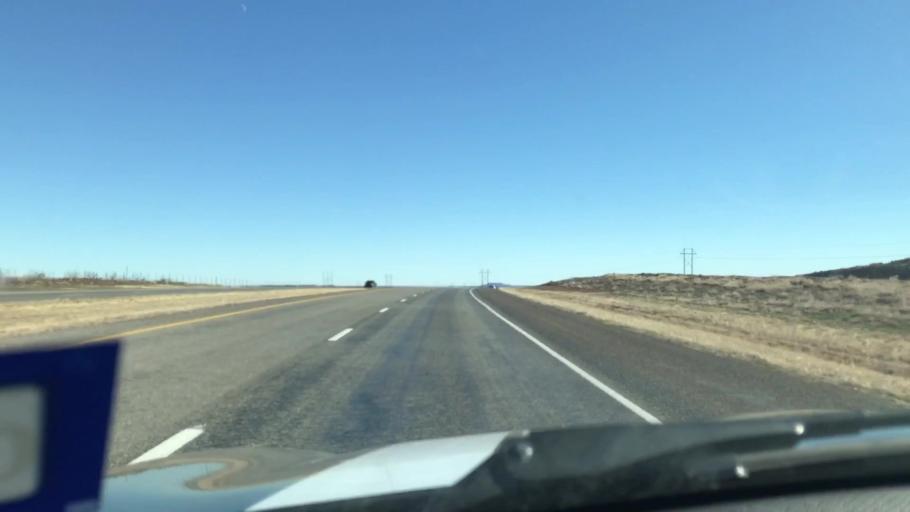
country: US
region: Texas
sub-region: Garza County
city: Post
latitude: 33.1194
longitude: -101.2806
